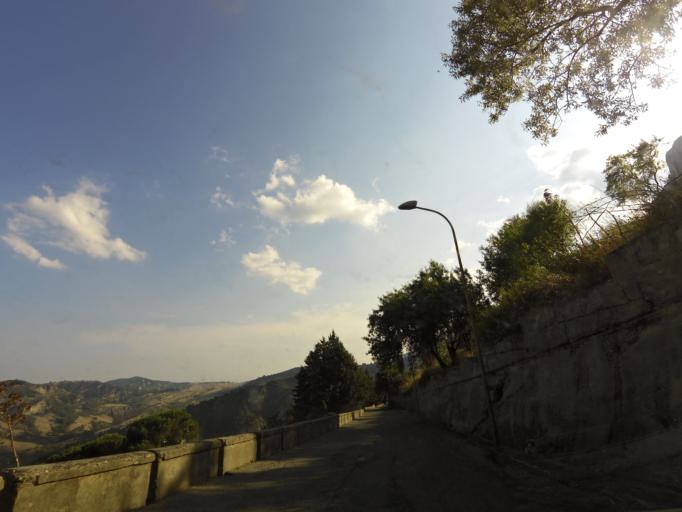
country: IT
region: Calabria
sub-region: Provincia di Reggio Calabria
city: Stilo
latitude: 38.4776
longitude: 16.4657
